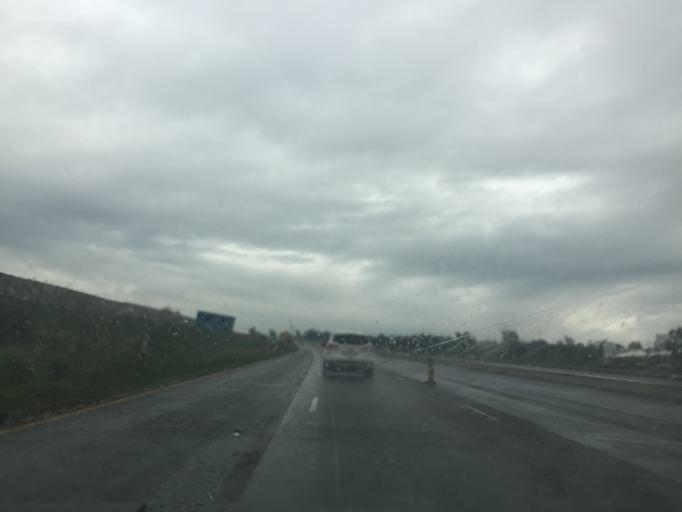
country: ZA
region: Gauteng
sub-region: City of Tshwane Metropolitan Municipality
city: Centurion
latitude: -25.8939
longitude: 28.0981
